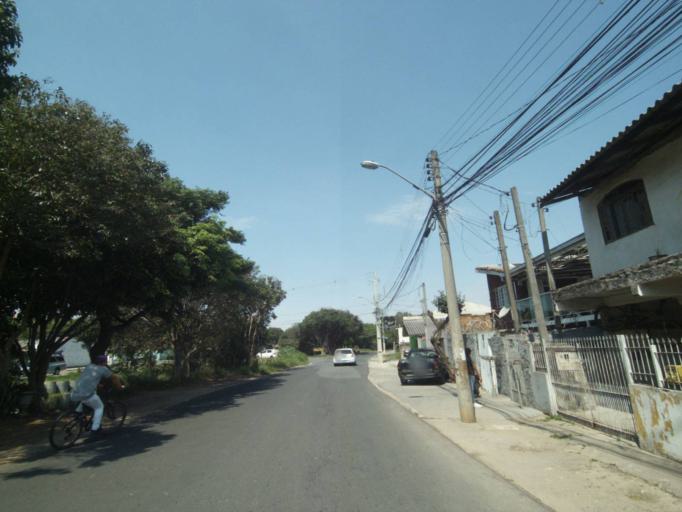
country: BR
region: Parana
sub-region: Curitiba
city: Curitiba
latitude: -25.4782
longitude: -49.3189
